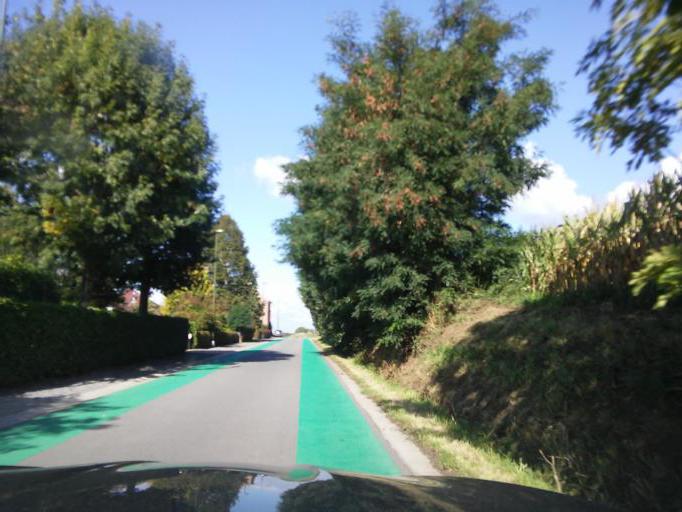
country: BE
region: Flanders
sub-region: Provincie Vlaams-Brabant
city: Pepingen
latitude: 50.7335
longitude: 4.1628
